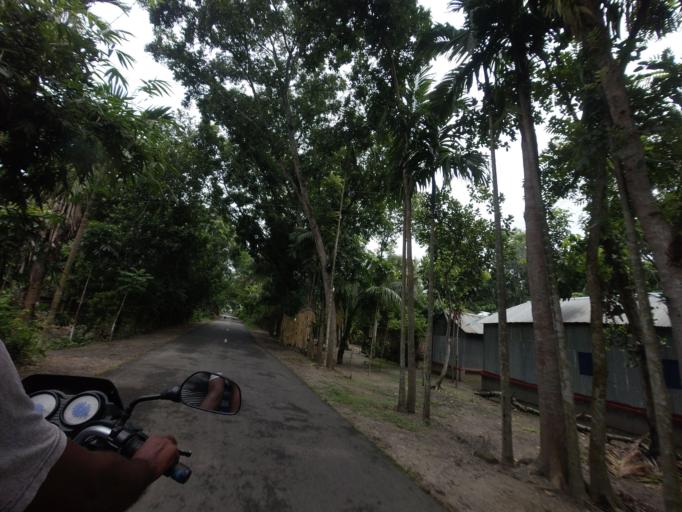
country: BD
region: Khulna
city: Kalia
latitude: 23.0971
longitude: 89.6524
